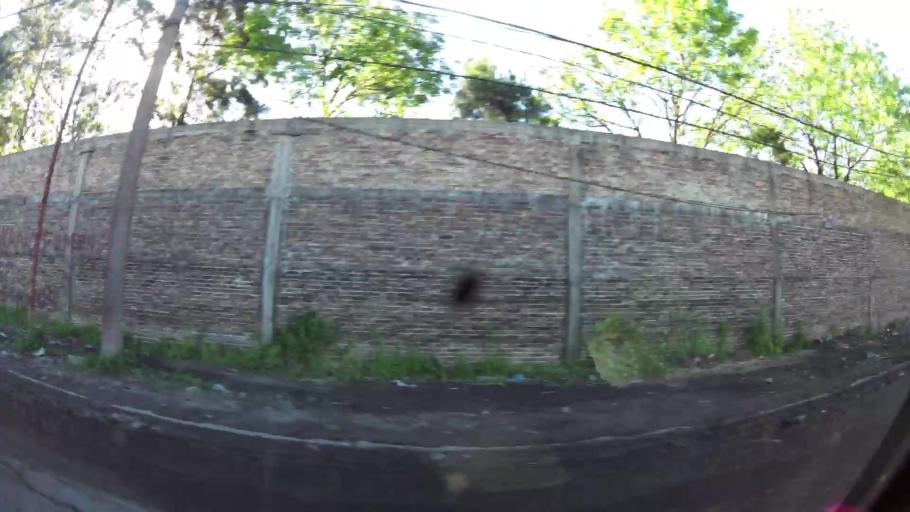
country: AR
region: Buenos Aires
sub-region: Partido de Quilmes
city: Quilmes
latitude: -34.7488
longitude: -58.3136
